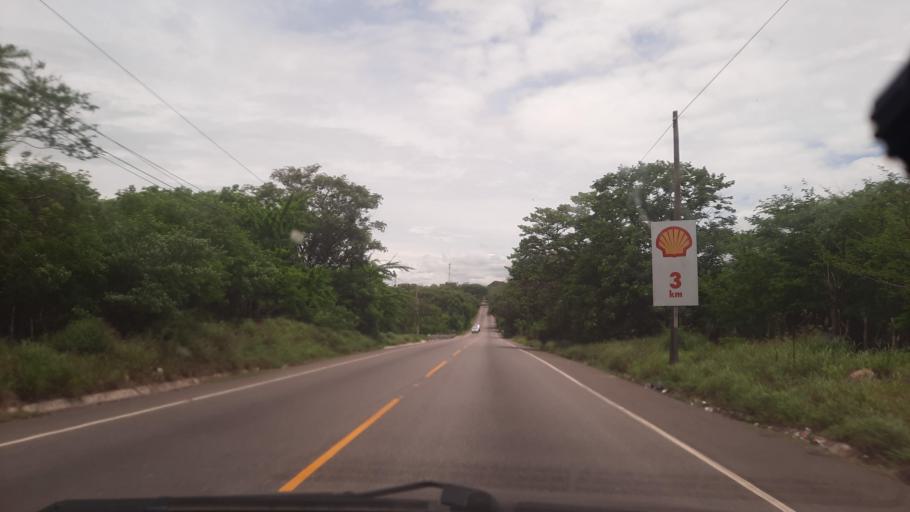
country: GT
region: Zacapa
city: Rio Hondo
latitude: 15.0566
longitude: -89.5512
